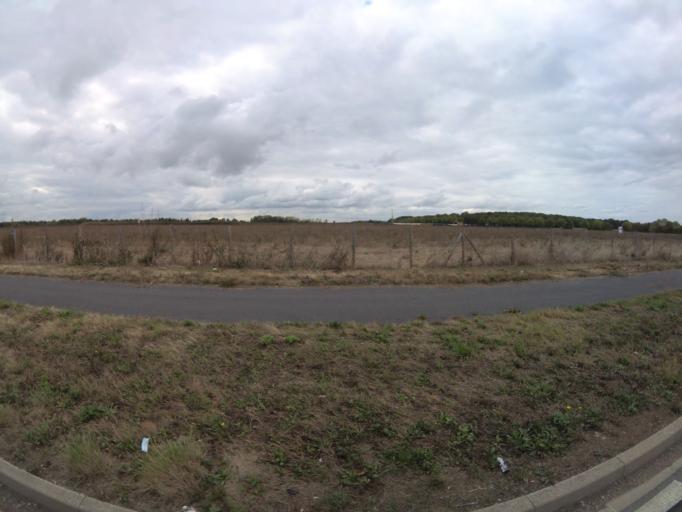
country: FR
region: Ile-de-France
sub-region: Departement de Seine-et-Marne
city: Coupvray
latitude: 48.8799
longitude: 2.8058
